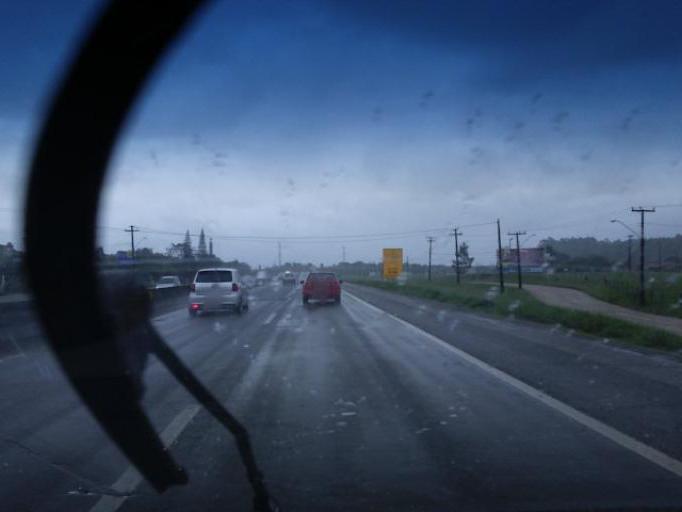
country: BR
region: Santa Catarina
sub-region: Barra Velha
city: Barra Velha
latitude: -26.5261
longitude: -48.7156
